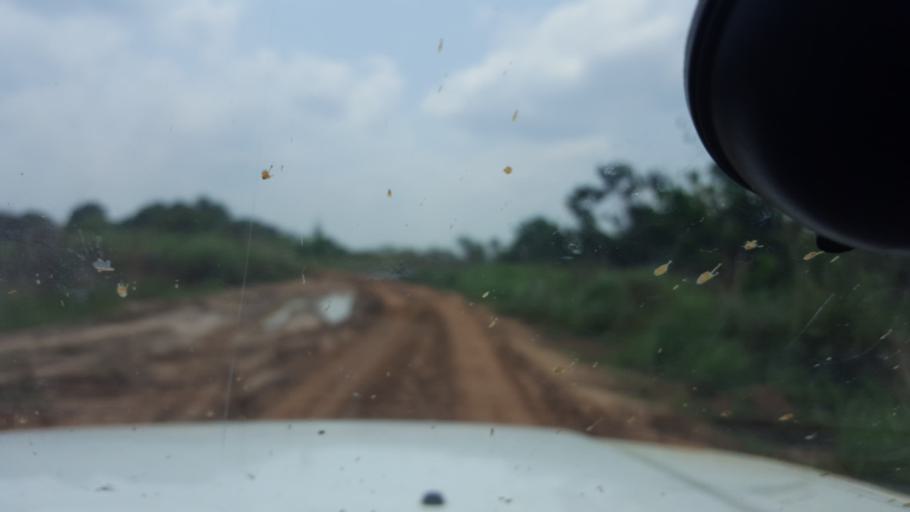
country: CD
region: Bandundu
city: Mushie
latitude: -3.7510
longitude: 16.6462
